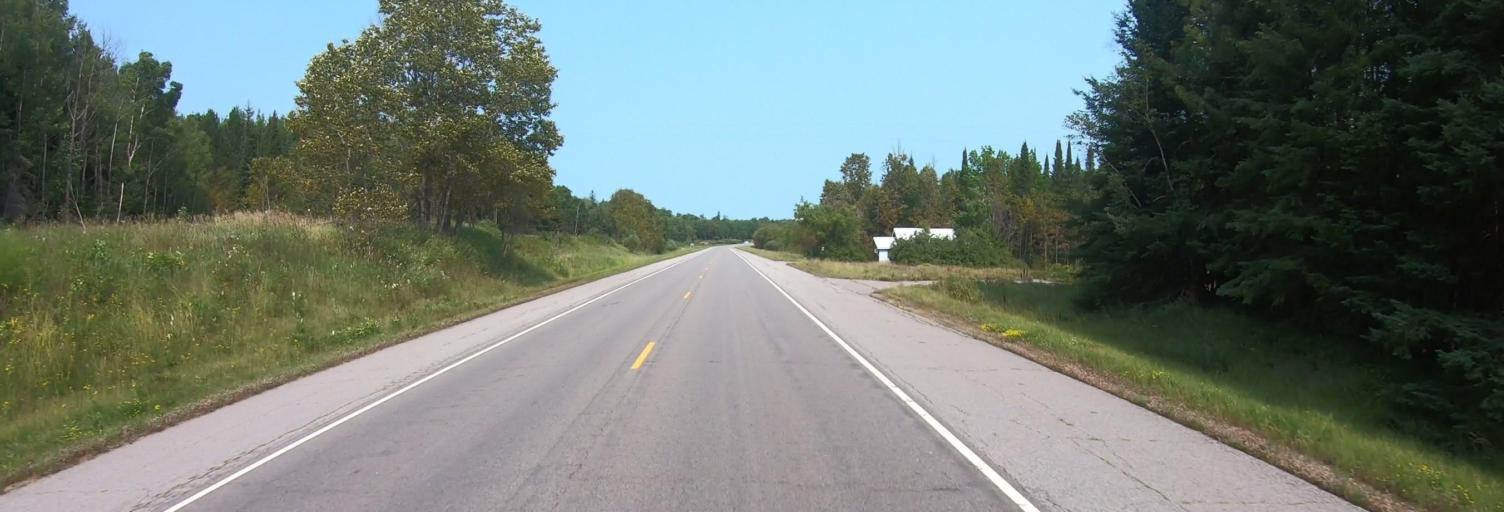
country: CA
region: Ontario
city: Fort Frances
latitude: 48.2254
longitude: -92.9231
